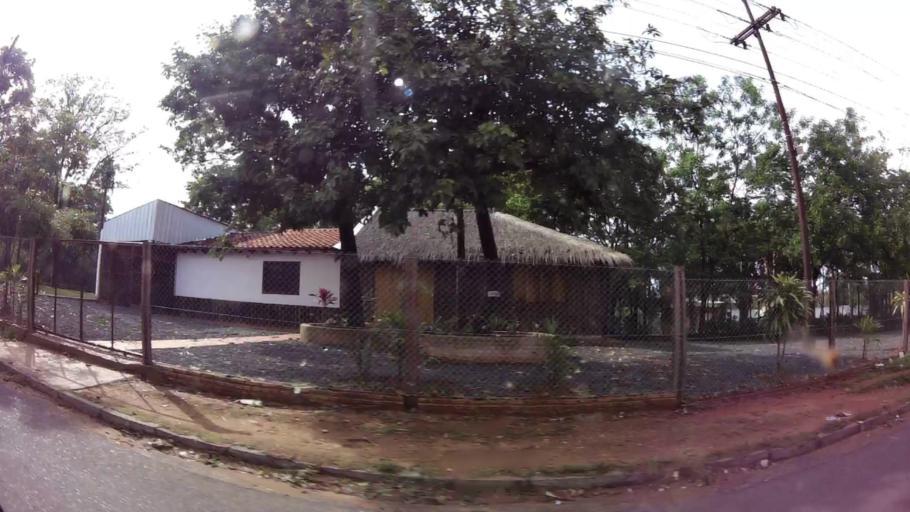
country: PY
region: Central
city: Limpio
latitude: -25.1658
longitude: -57.4683
